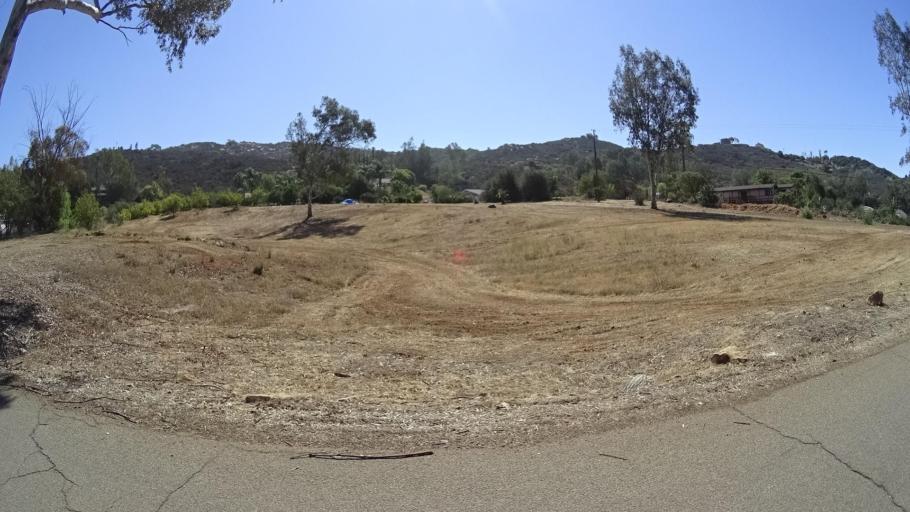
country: US
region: California
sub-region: San Diego County
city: Rainbow
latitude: 33.4251
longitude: -117.1718
